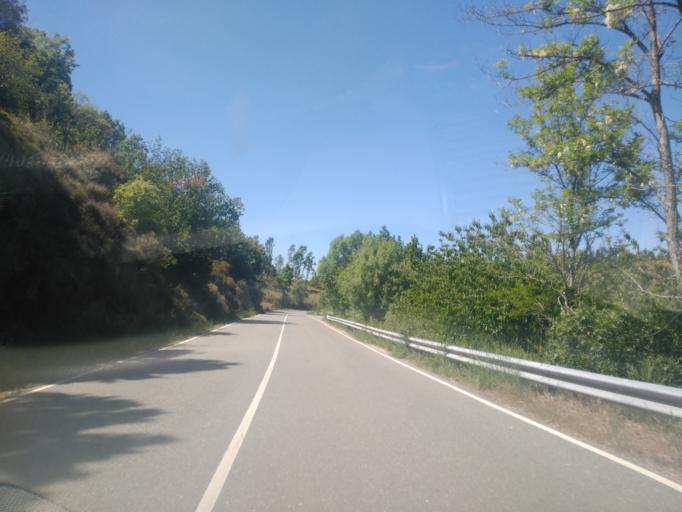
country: ES
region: Castille and Leon
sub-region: Provincia de Salamanca
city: Candelario
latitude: 40.3786
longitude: -5.7478
